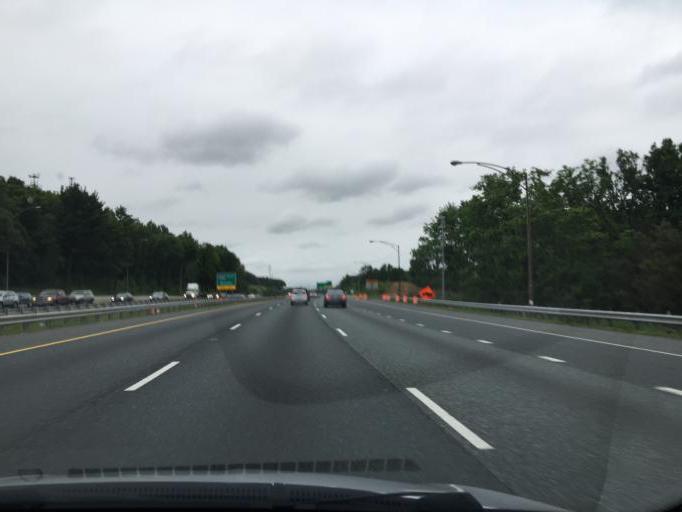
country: US
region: Maryland
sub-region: Baltimore County
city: Overlea
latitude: 39.3663
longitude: -76.5096
